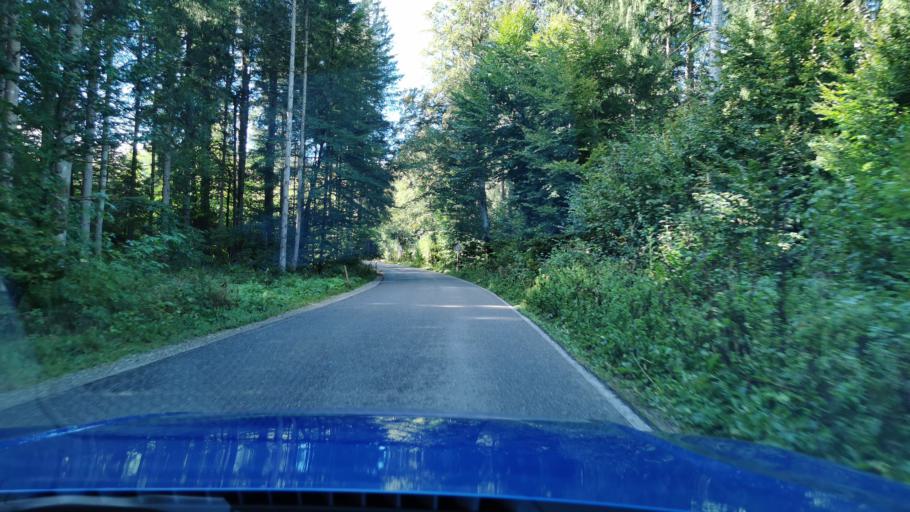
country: DE
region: Bavaria
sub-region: Upper Bavaria
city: Warngau
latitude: 47.8155
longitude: 11.6952
